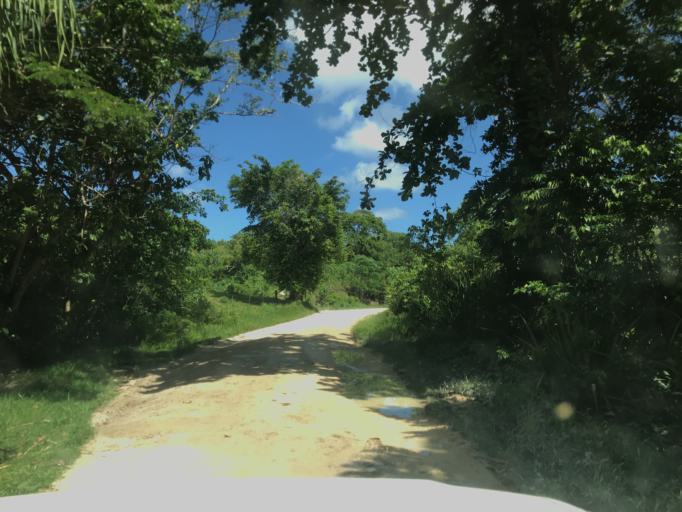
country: VU
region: Sanma
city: Luganville
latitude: -15.5788
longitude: 167.0357
